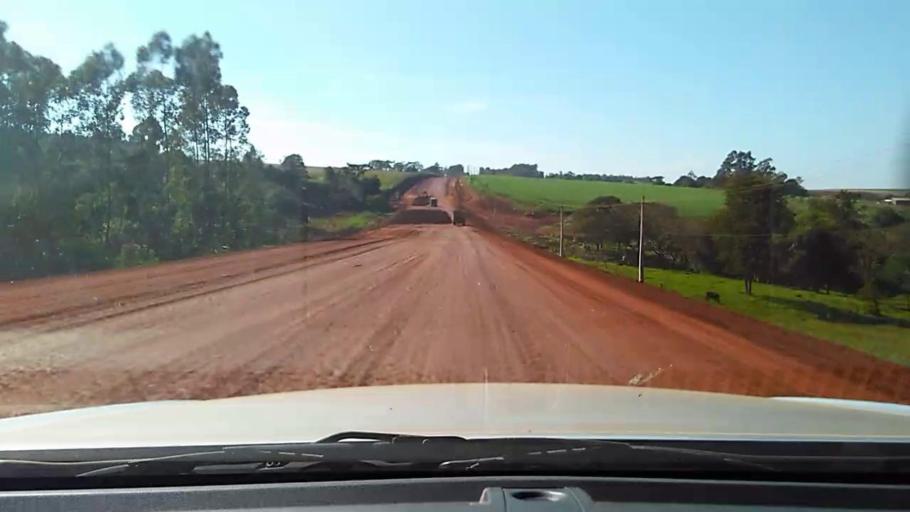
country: PY
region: Alto Parana
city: Naranjal
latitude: -25.9233
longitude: -55.4069
